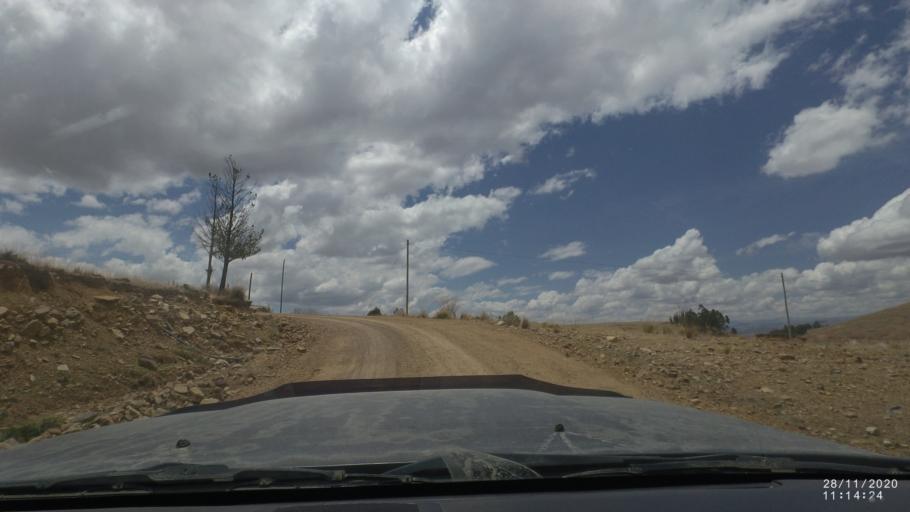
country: BO
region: Cochabamba
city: Tarata
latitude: -17.7462
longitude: -66.0976
